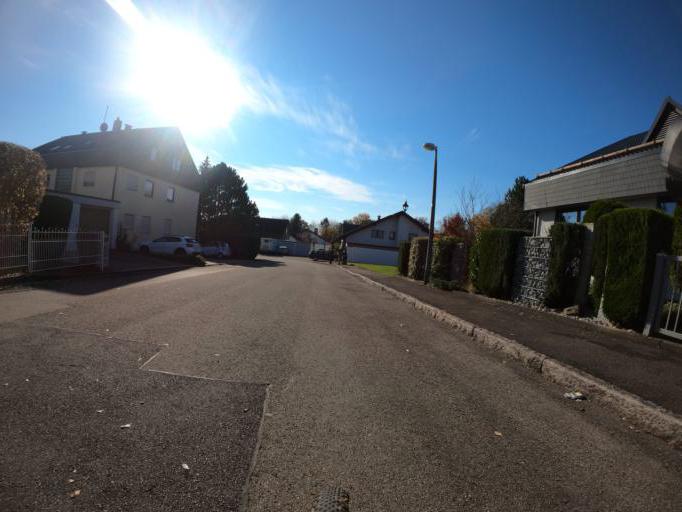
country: DE
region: Baden-Wuerttemberg
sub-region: Regierungsbezirk Stuttgart
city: Magstadt
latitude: 48.7209
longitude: 8.9586
